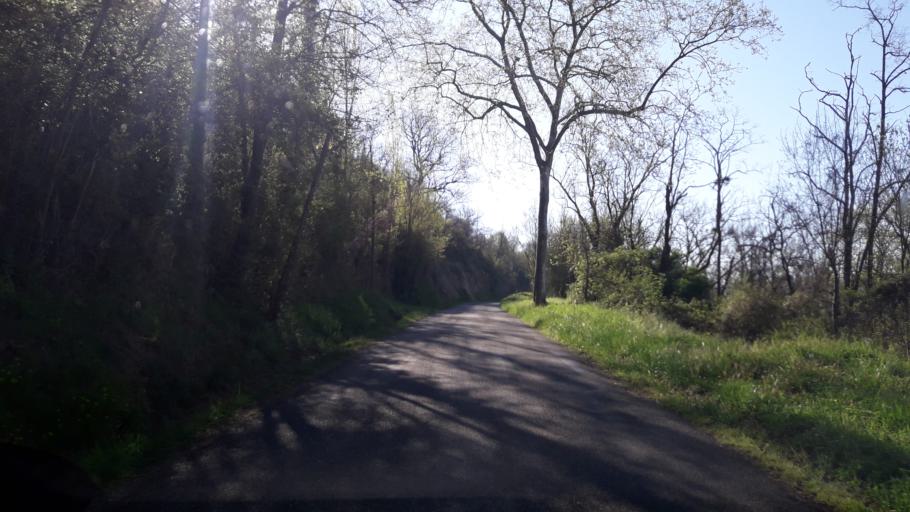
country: FR
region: Midi-Pyrenees
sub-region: Departement de la Haute-Garonne
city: Montesquieu-Volvestre
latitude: 43.1992
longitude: 1.2439
